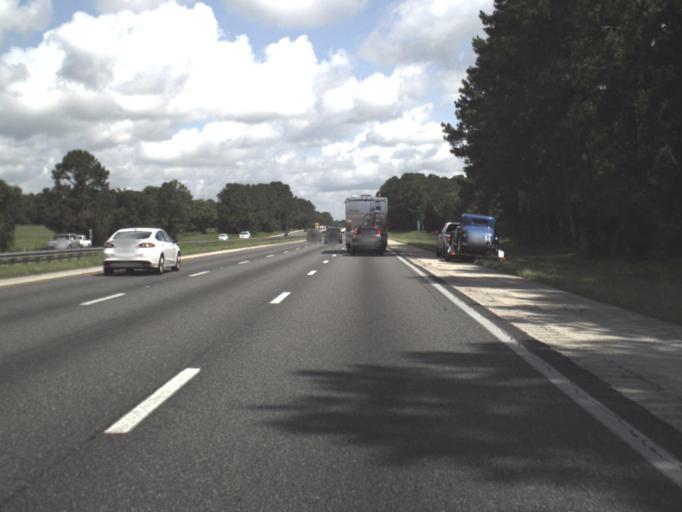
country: US
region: Florida
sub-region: Alachua County
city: High Springs
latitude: 29.8287
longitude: -82.5221
